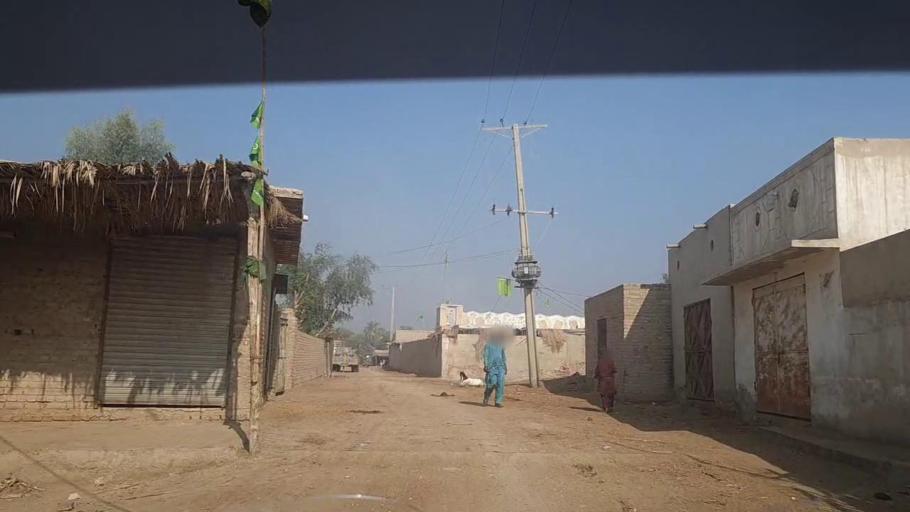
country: PK
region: Sindh
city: Khairpur
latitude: 27.4700
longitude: 68.7132
